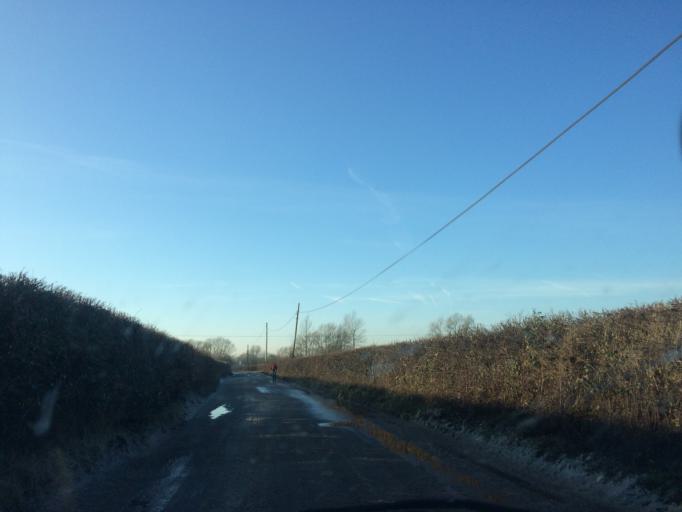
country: GB
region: England
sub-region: Wiltshire
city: Leigh
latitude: 51.6383
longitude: -1.9110
